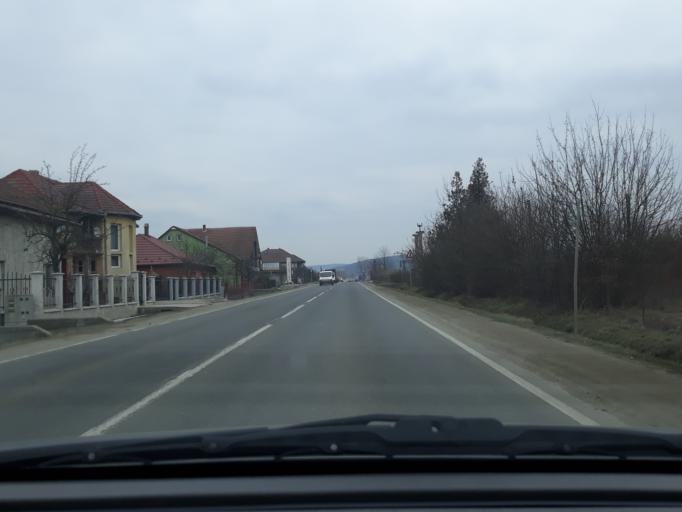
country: RO
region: Salaj
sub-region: Comuna Hereclean
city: Hereclean
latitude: 47.2251
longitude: 23.0128
